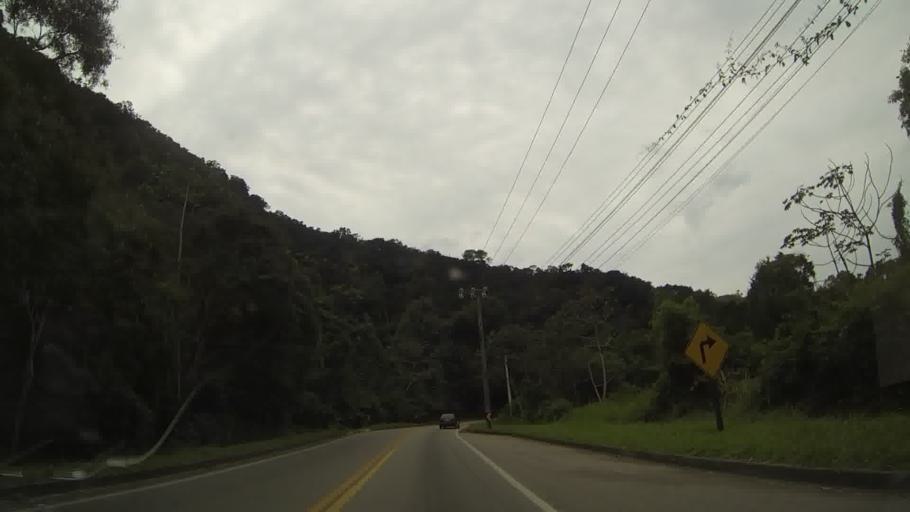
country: BR
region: Sao Paulo
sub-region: Sao Sebastiao
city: Sao Sebastiao
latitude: -23.8229
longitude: -45.4446
